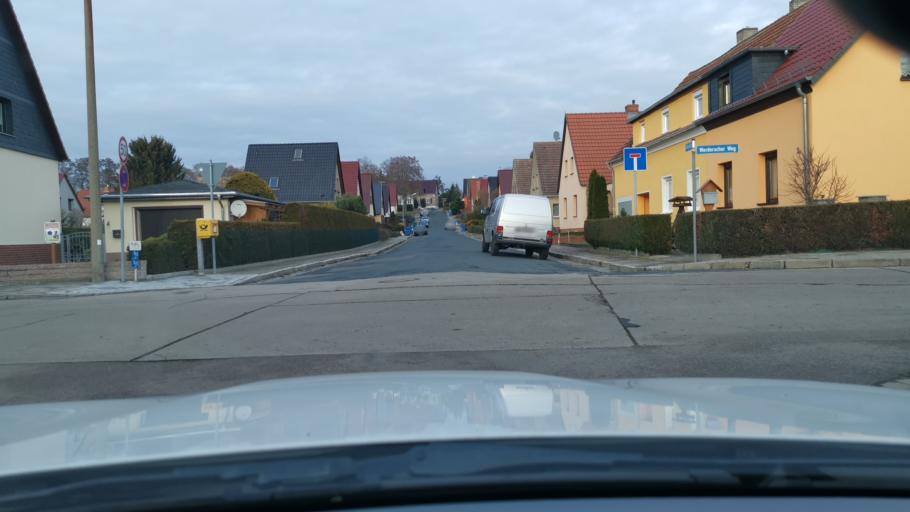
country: DE
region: Brandenburg
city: Juterbog
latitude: 52.0003
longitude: 13.0907
